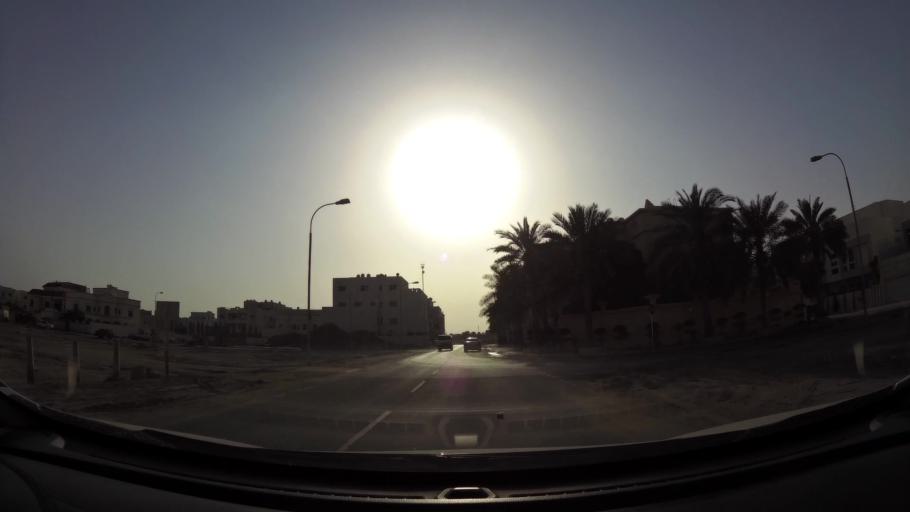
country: BH
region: Manama
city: Jidd Hafs
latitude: 26.2093
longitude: 50.5007
